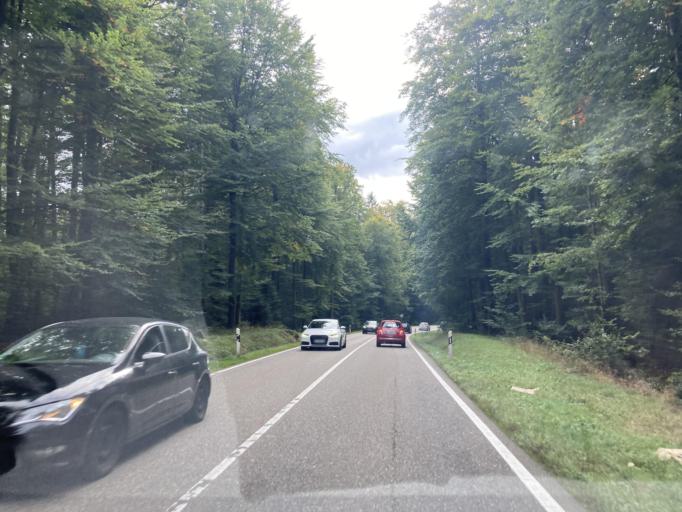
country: DE
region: Baden-Wuerttemberg
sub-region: Karlsruhe Region
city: Neuenburg
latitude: 48.8586
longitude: 8.6089
